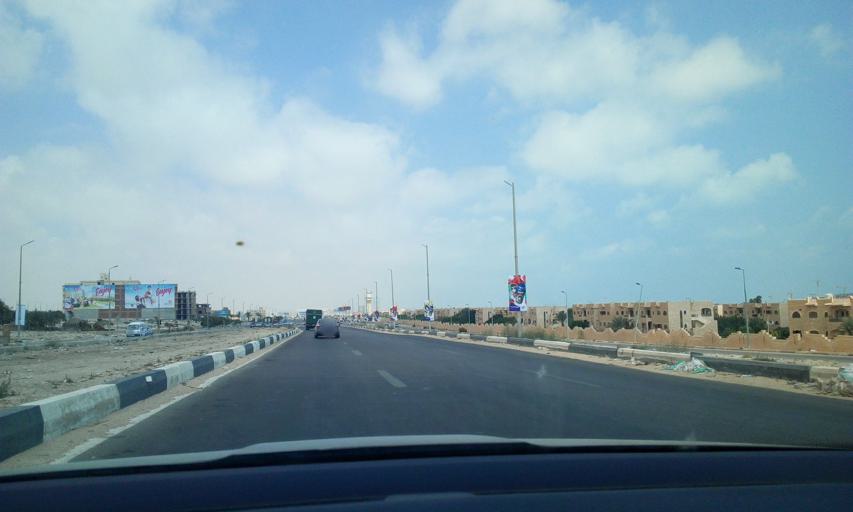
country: EG
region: Muhafazat Matruh
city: Al `Alamayn
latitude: 30.8367
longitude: 28.9575
